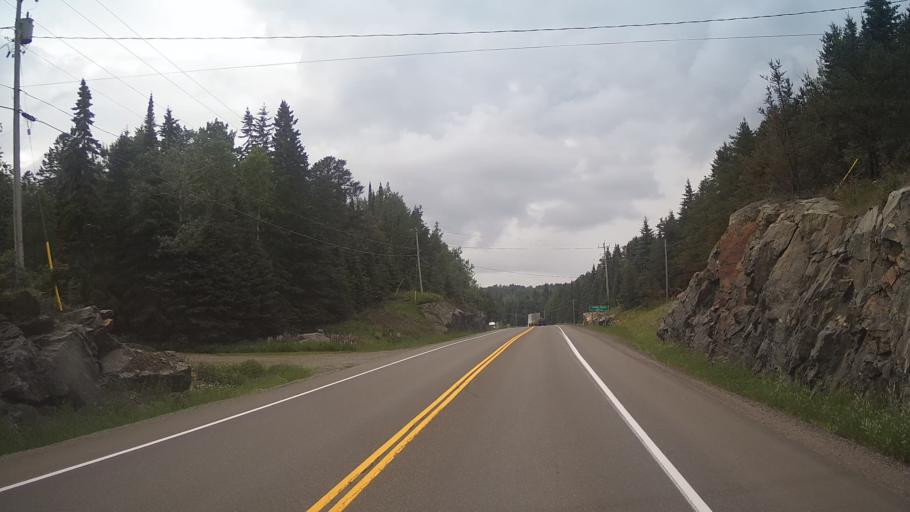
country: CA
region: Ontario
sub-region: Thunder Bay District
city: Thunder Bay
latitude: 48.5027
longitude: -89.4440
